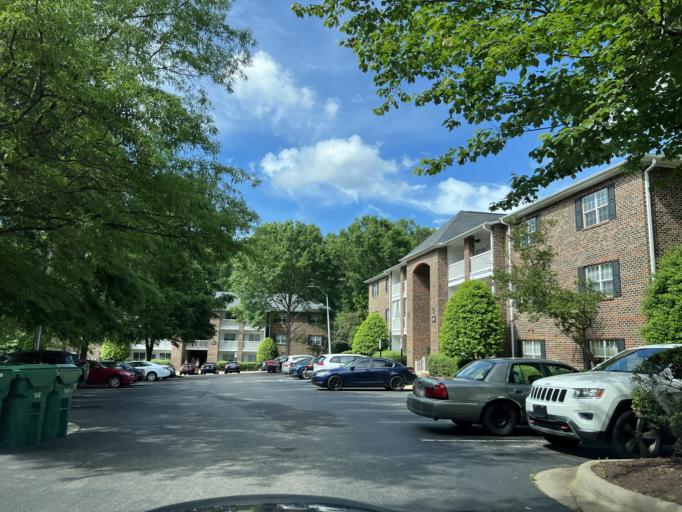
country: US
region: North Carolina
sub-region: Wake County
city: Wake Forest
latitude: 35.8867
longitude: -78.5896
